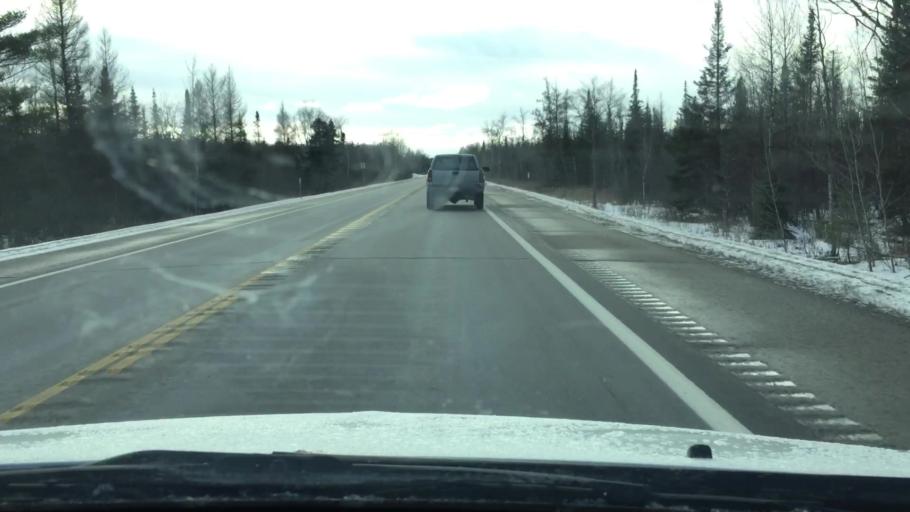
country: US
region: Michigan
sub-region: Kalkaska County
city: Kalkaska
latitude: 44.6622
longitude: -85.2508
